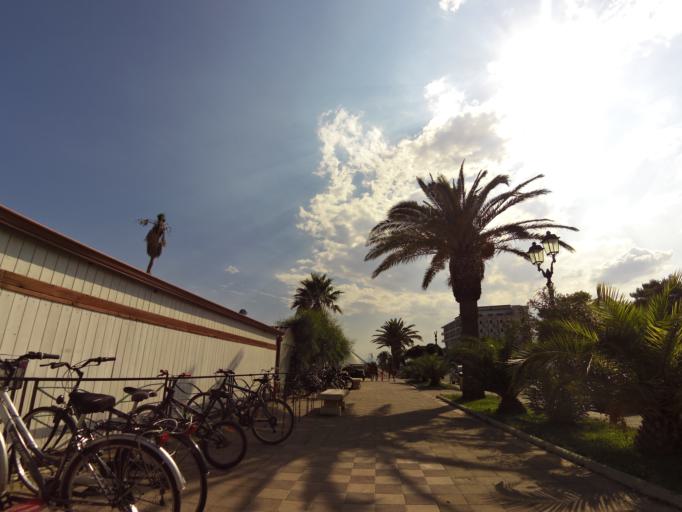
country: IT
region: Calabria
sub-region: Provincia di Reggio Calabria
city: Siderno
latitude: 38.2662
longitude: 16.2974
